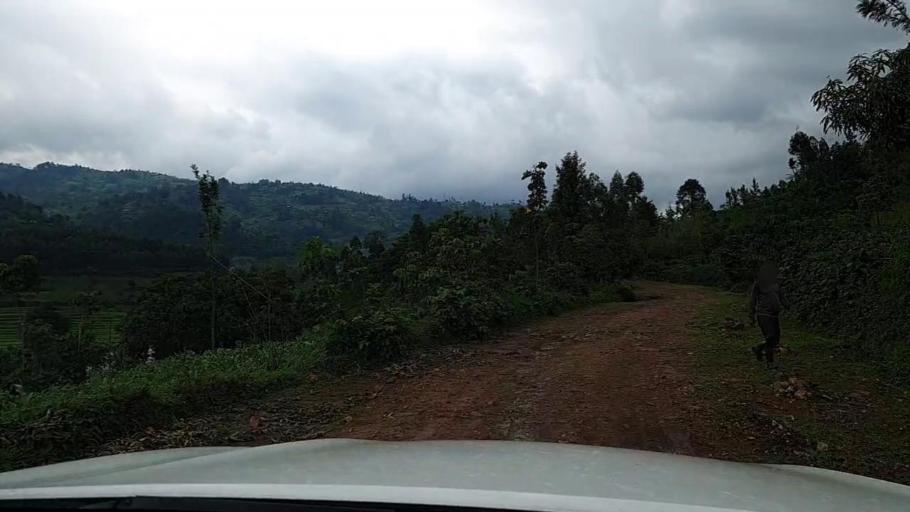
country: RW
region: Western Province
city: Cyangugu
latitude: -2.5603
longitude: 29.0357
